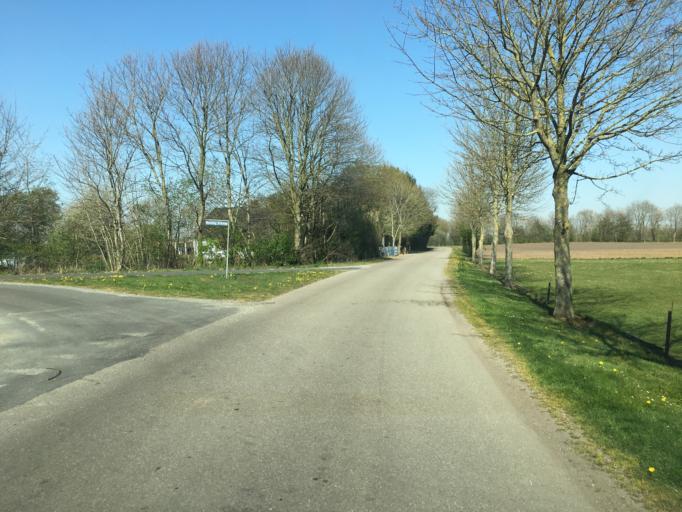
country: DK
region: South Denmark
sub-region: Aabenraa Kommune
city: Rodekro
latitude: 55.0764
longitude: 9.2544
